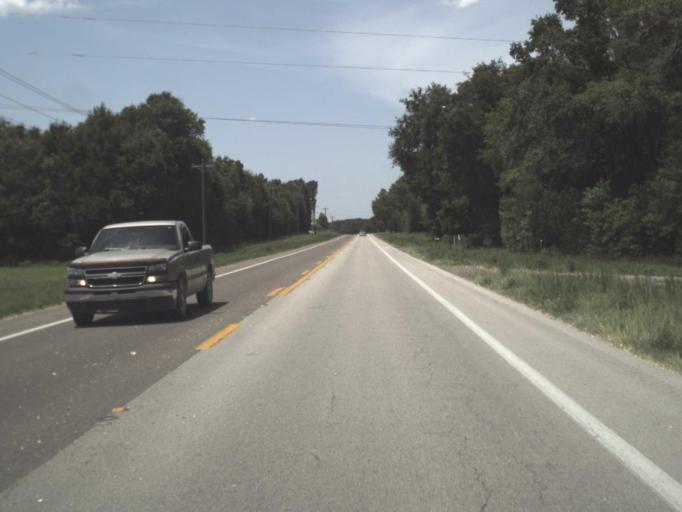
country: US
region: Florida
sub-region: Gilchrist County
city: Trenton
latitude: 29.7328
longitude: -82.8578
